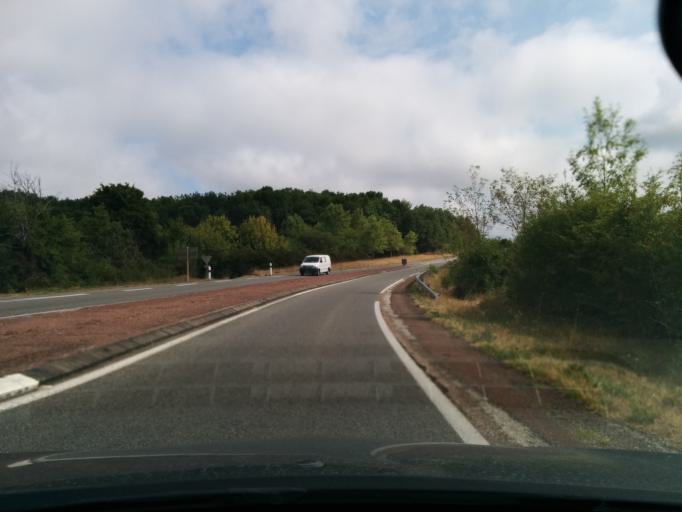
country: FR
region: Midi-Pyrenees
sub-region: Departement du Lot
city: Pradines
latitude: 44.5659
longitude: 1.4721
